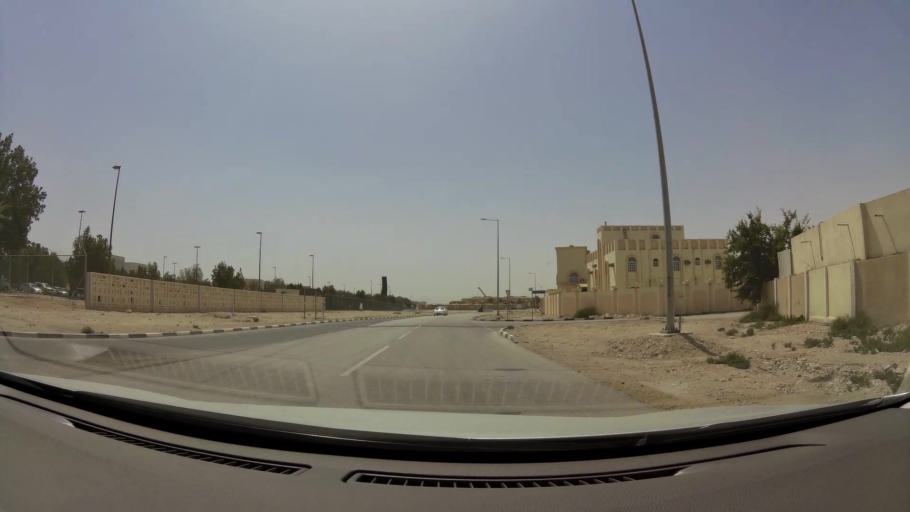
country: QA
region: Baladiyat ar Rayyan
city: Ar Rayyan
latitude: 25.3624
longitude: 51.4790
